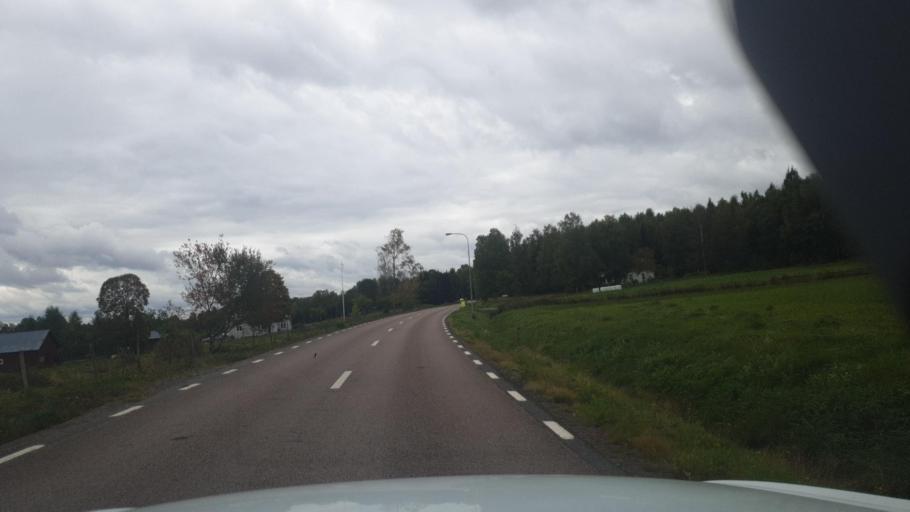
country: SE
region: Vaermland
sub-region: Sunne Kommun
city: Sunne
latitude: 59.8941
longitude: 12.9191
